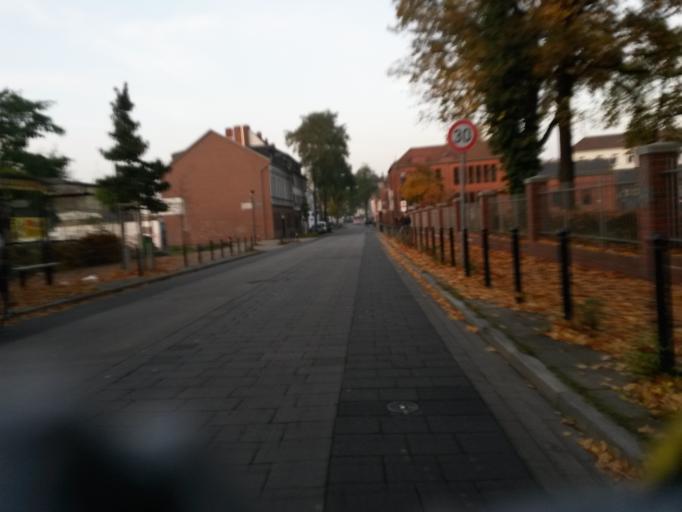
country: DE
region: Bremen
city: Bremen
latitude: 53.0582
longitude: 8.8855
